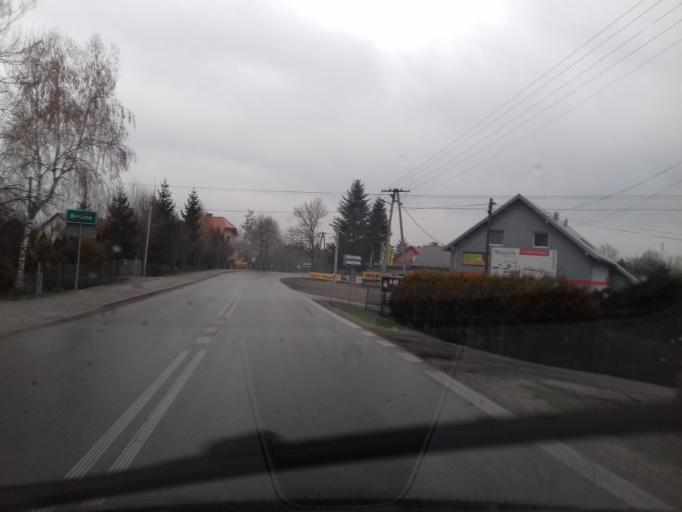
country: PL
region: Lesser Poland Voivodeship
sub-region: Powiat nowosadecki
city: Stary Sacz
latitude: 49.5975
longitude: 20.6363
